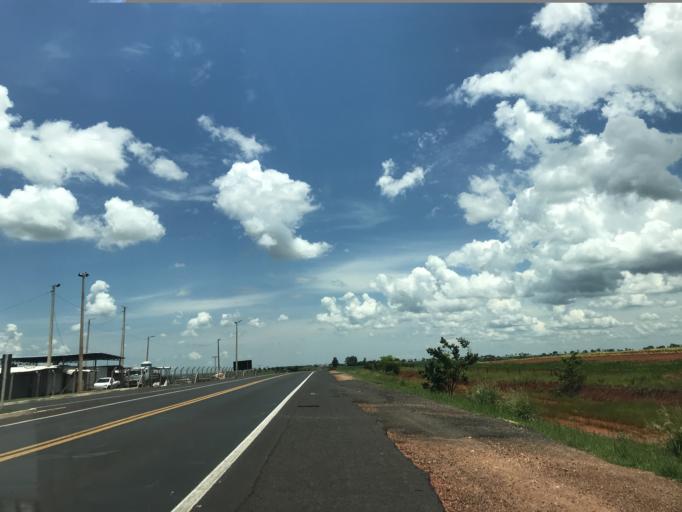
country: BR
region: Minas Gerais
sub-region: Prata
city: Prata
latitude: -19.4966
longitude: -48.8536
